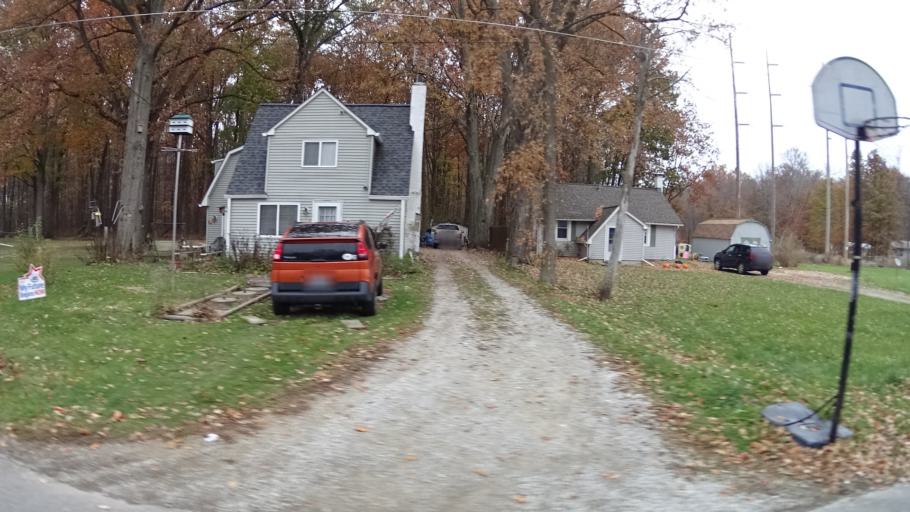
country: US
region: Ohio
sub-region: Lorain County
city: Elyria
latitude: 41.3314
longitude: -82.1135
